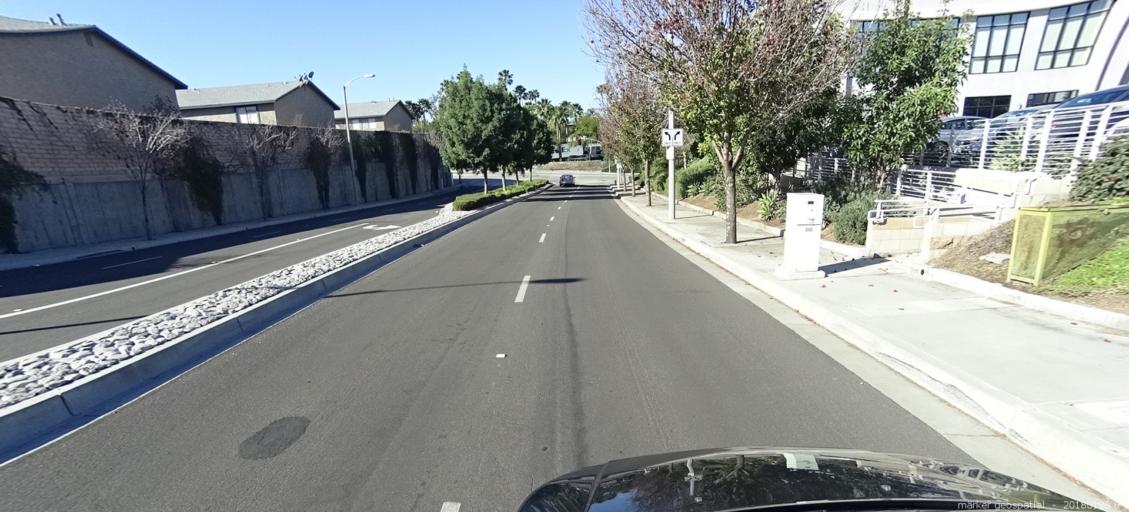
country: US
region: California
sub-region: Los Angeles County
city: Walnut
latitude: 34.0066
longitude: -117.8455
